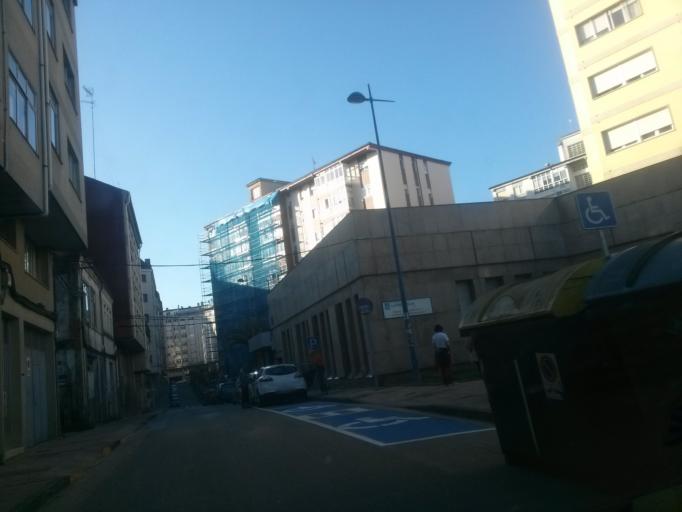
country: ES
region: Galicia
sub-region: Provincia de Lugo
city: Lugo
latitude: 43.0173
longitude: -7.5597
